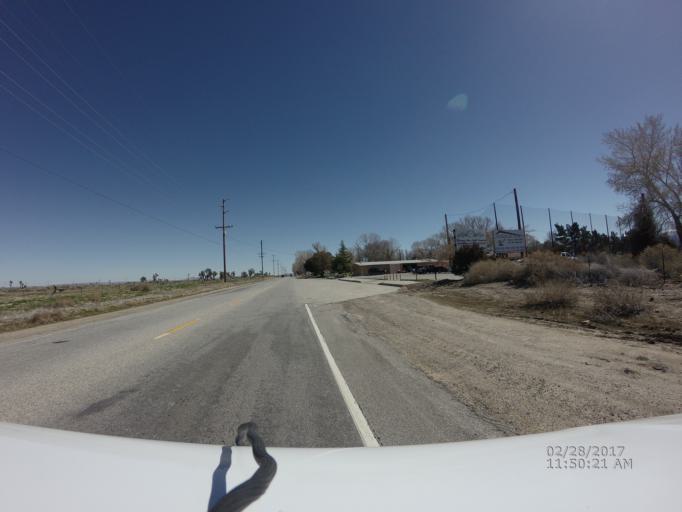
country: US
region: California
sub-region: Los Angeles County
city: Palmdale
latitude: 34.6021
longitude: -118.0655
